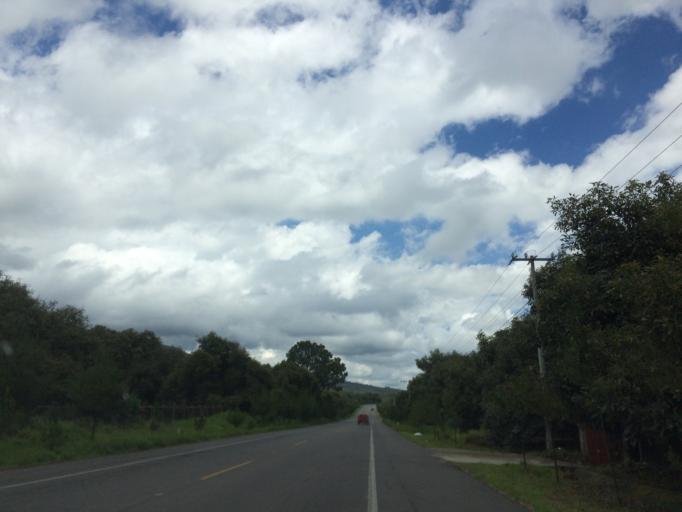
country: MX
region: Michoacan
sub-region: Uruapan
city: Santa Ana Zirosto
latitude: 19.5454
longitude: -102.3192
